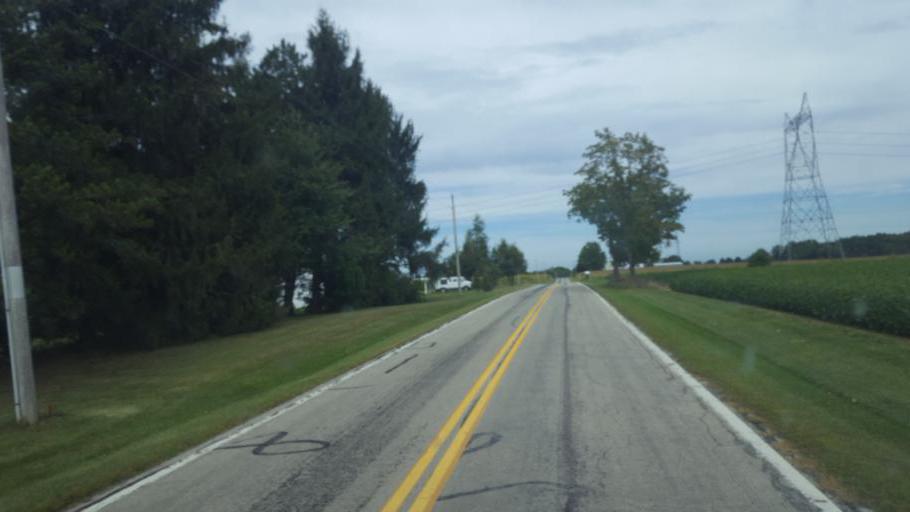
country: US
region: Ohio
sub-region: Knox County
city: Centerburg
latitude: 40.2695
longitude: -82.7513
